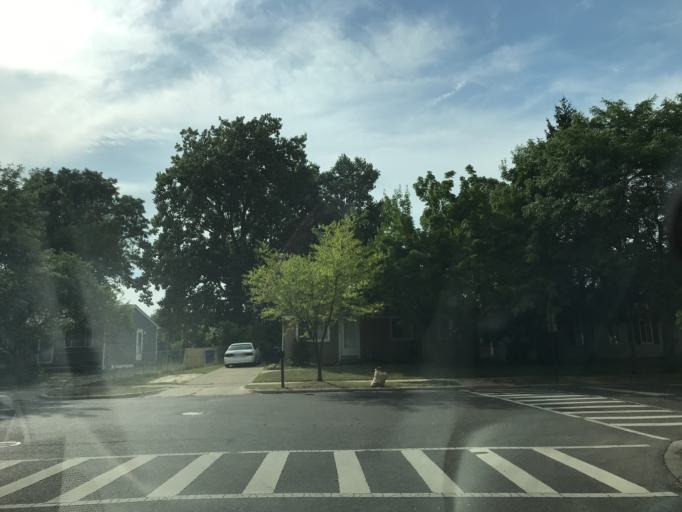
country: US
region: Michigan
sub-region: Washtenaw County
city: Ann Arbor
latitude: 42.2334
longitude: -83.7169
